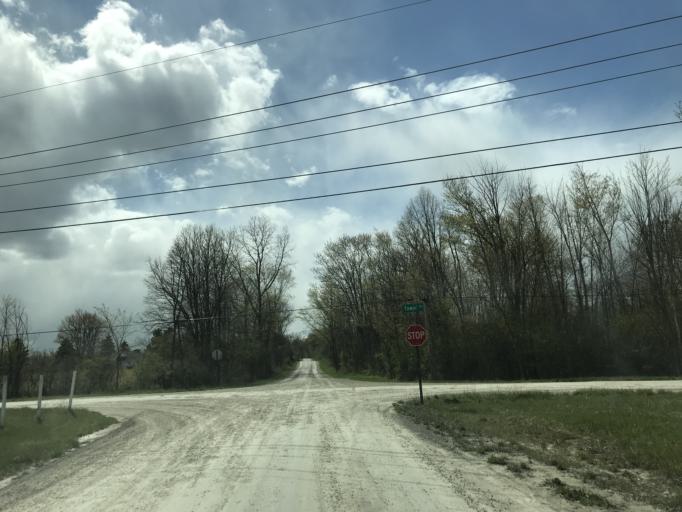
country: US
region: Michigan
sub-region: Oakland County
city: South Lyon
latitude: 42.3761
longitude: -83.6268
